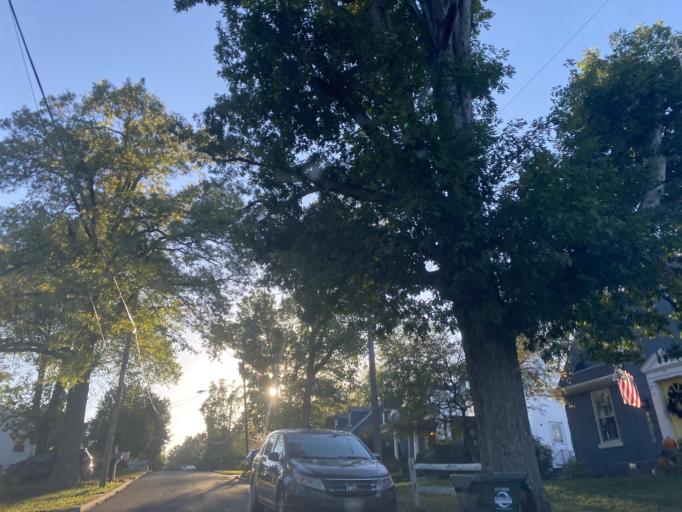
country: US
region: Kentucky
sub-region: Campbell County
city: Fort Thomas
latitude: 39.1004
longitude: -84.4473
